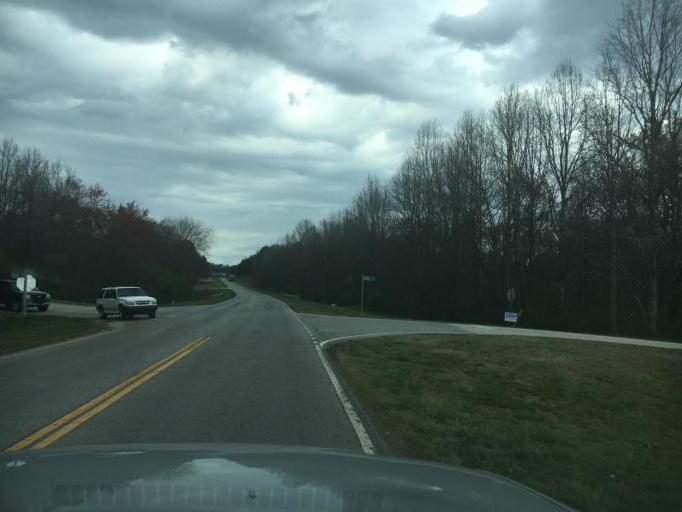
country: US
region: South Carolina
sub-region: Oconee County
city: Walhalla
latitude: 34.7433
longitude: -83.0497
